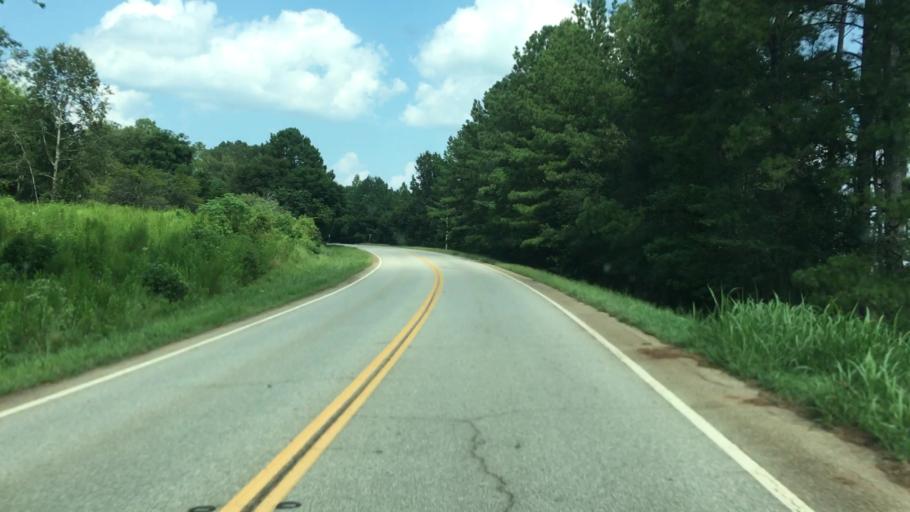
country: US
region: Georgia
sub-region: Monroe County
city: Forsyth
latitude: 33.1029
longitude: -83.8788
